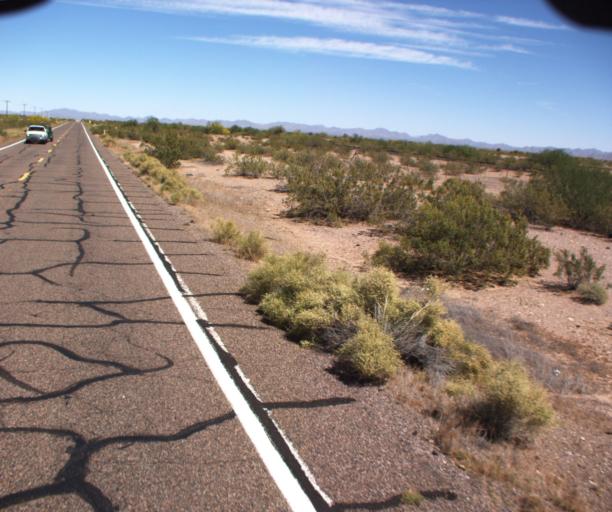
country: US
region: Arizona
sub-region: Maricopa County
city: Gila Bend
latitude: 32.8861
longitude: -112.7512
